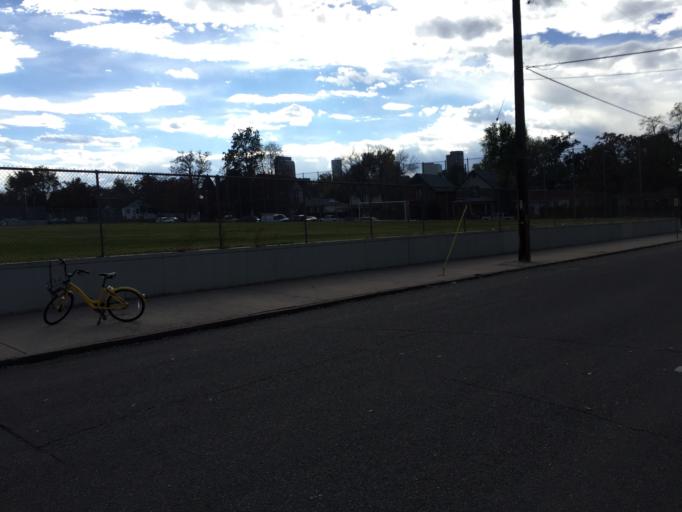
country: US
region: Colorado
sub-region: Denver County
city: Denver
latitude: 39.7570
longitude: -104.9688
